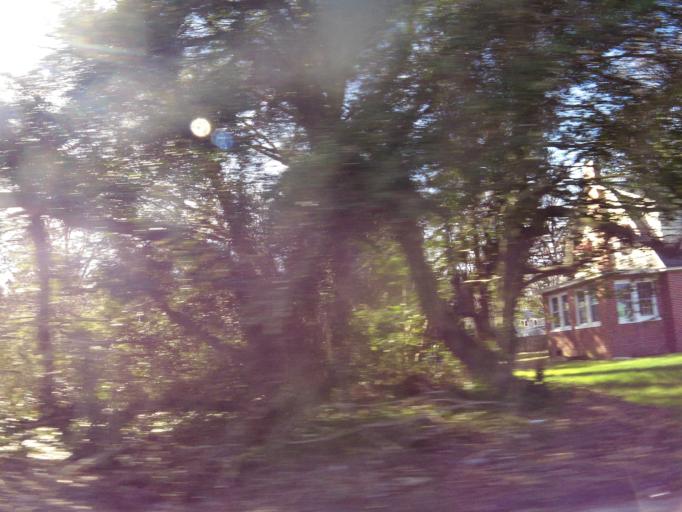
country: US
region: Virginia
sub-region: City of Newport News
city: Newport News
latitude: 37.0392
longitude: -76.4686
